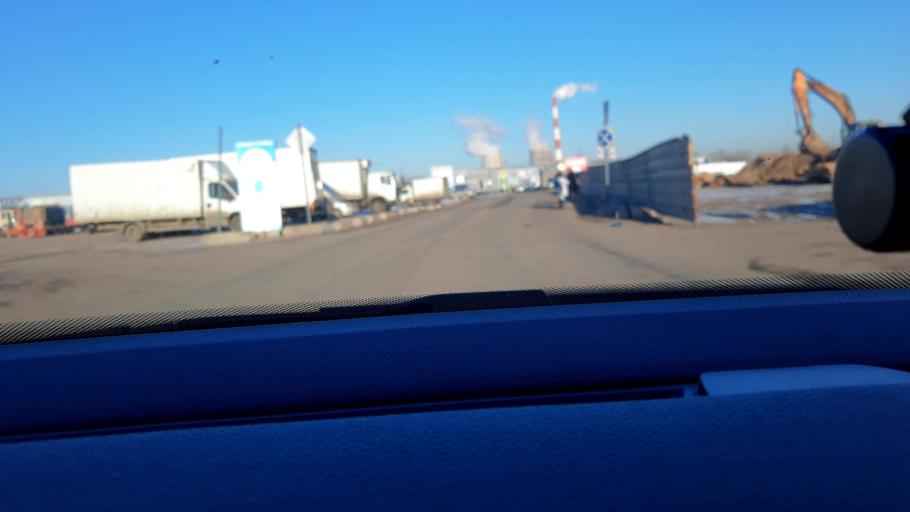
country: RU
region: Moscow
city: Vatutino
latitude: 55.8984
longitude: 37.6805
